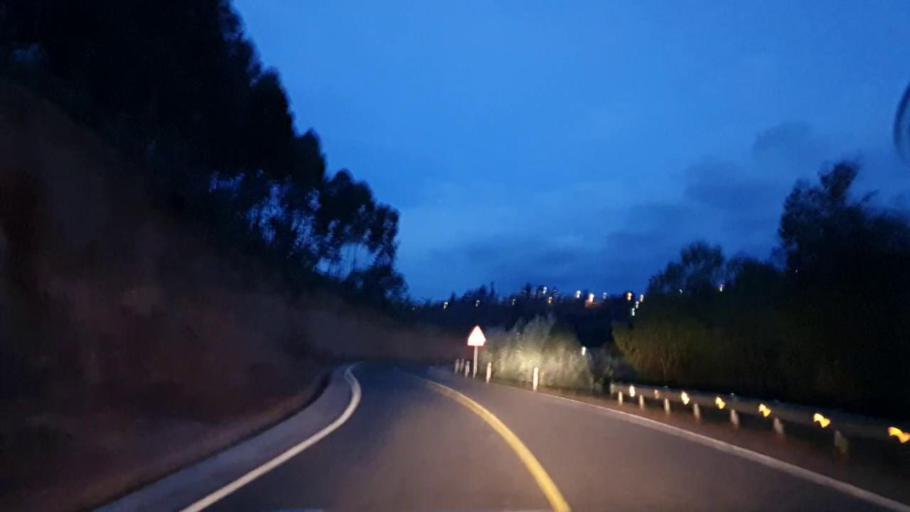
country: RW
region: Southern Province
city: Gikongoro
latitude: -2.4643
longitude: 29.5660
